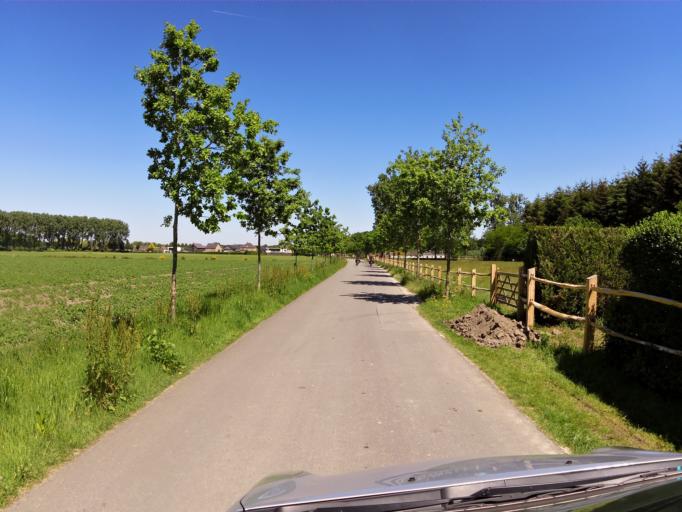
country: BE
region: Flanders
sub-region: Provincie West-Vlaanderen
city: Zedelgem
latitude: 51.1774
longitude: 3.1707
